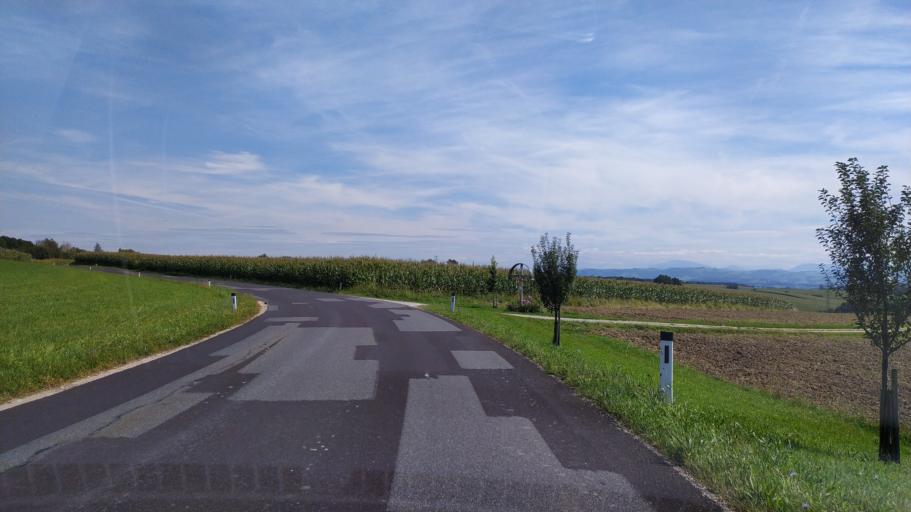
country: AT
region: Lower Austria
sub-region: Politischer Bezirk Amstetten
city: Wolfsbach
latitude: 48.1153
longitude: 14.7163
